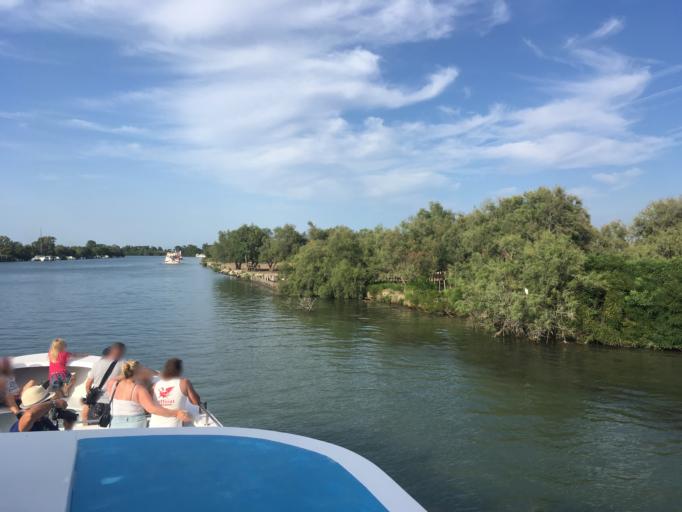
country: FR
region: Provence-Alpes-Cote d'Azur
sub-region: Departement des Bouches-du-Rhone
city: Saintes-Maries-de-la-Mer
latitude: 43.4834
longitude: 4.3797
